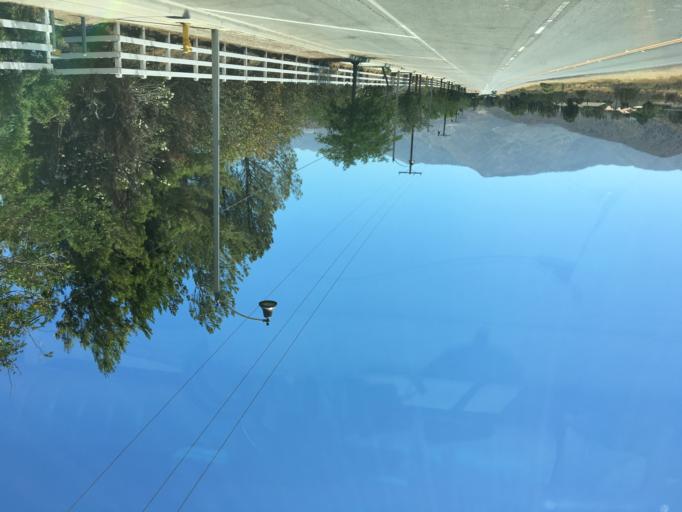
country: US
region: California
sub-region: Los Angeles County
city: Acton
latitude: 34.4802
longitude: -118.1982
